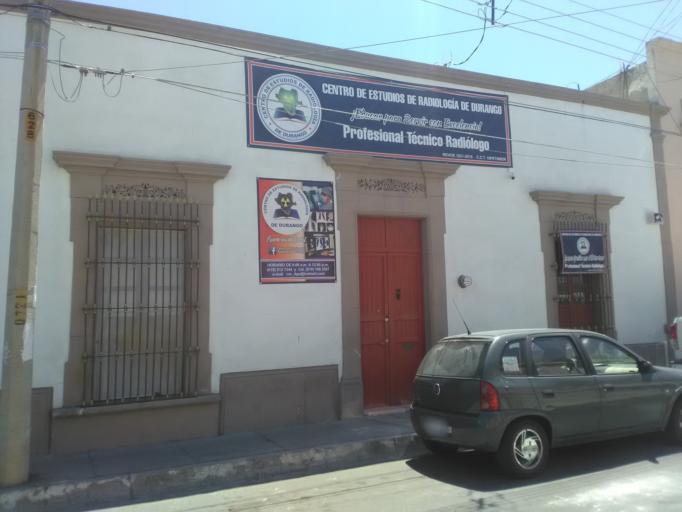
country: MX
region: Durango
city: Victoria de Durango
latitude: 24.0310
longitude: -104.6610
